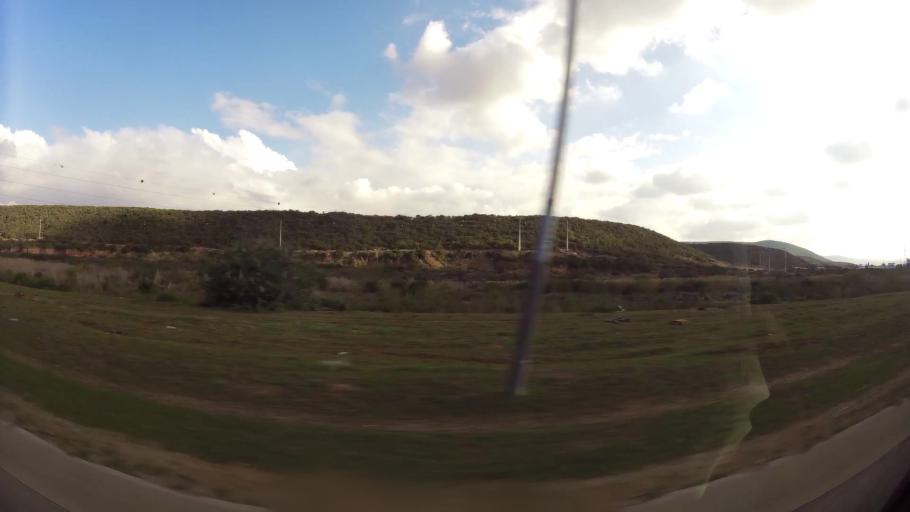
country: ZA
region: Eastern Cape
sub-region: Nelson Mandela Bay Metropolitan Municipality
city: Uitenhage
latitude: -33.7809
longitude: 25.3945
